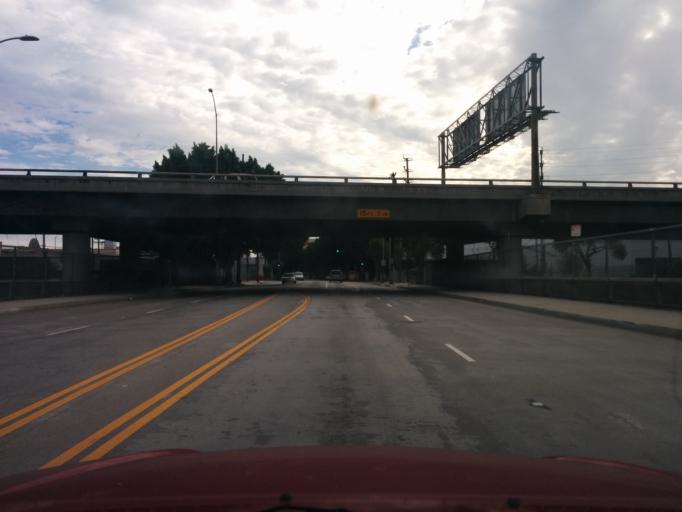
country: US
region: California
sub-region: Los Angeles County
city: Boyle Heights
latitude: 34.0298
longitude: -118.2205
